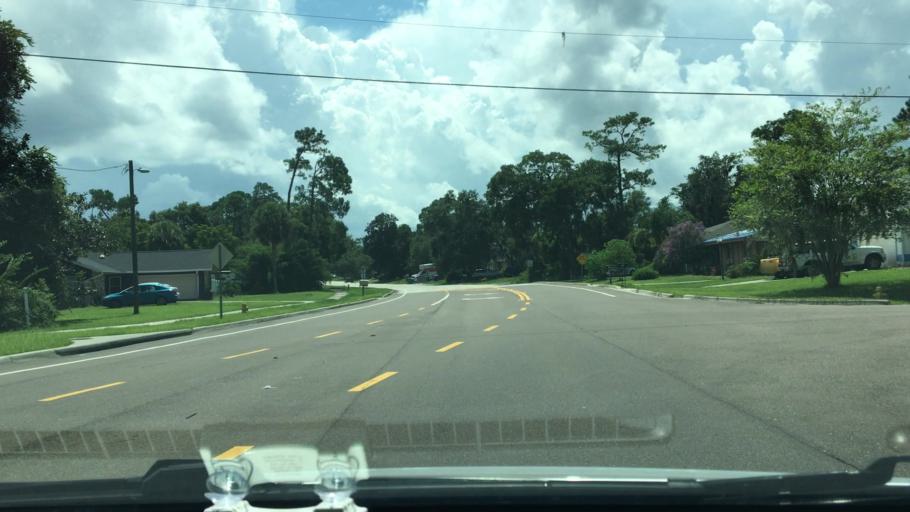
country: US
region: Florida
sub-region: Volusia County
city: Deltona
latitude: 28.8842
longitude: -81.2244
